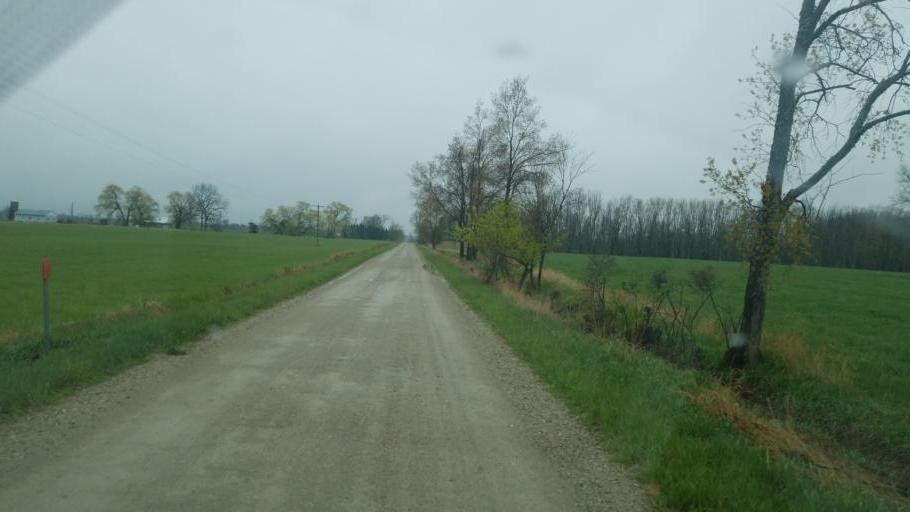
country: US
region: Michigan
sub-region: Montcalm County
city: Lakeview
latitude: 43.5027
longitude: -85.3187
